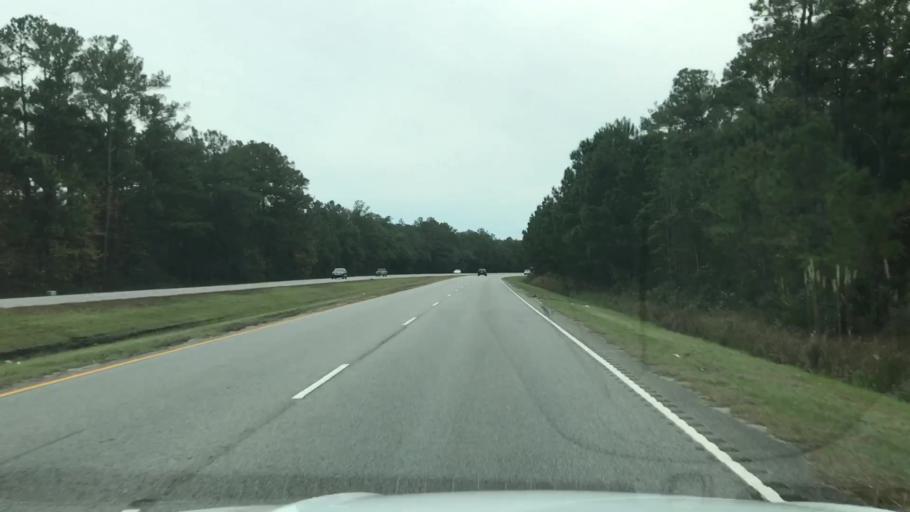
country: US
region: South Carolina
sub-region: Georgetown County
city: Georgetown
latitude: 33.3874
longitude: -79.2049
